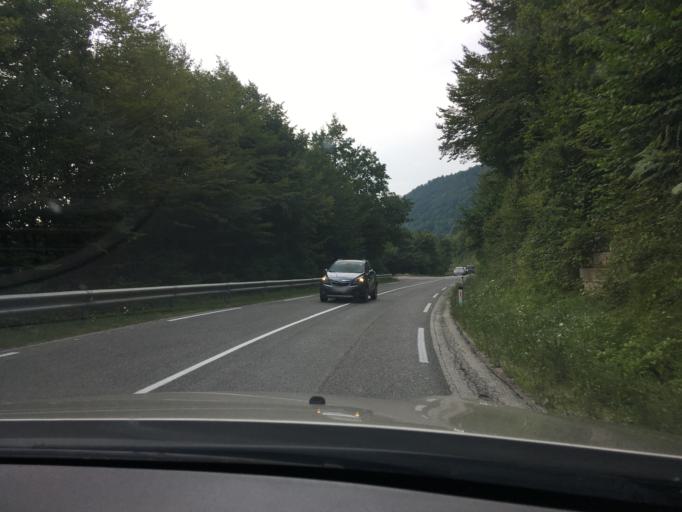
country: SI
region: Zuzemberk
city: Zuzemberk
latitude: 45.7903
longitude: 14.9892
